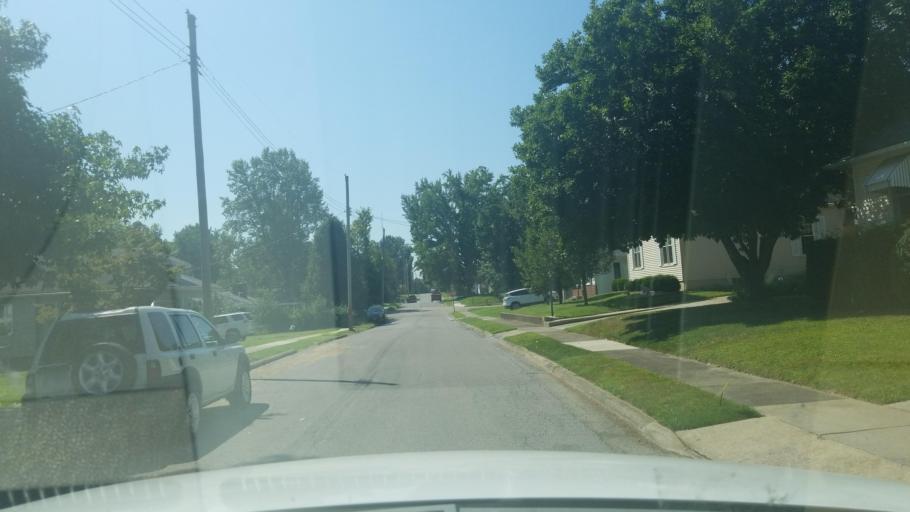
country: US
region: Illinois
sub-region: Saline County
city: Harrisburg
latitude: 37.7260
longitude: -88.5438
